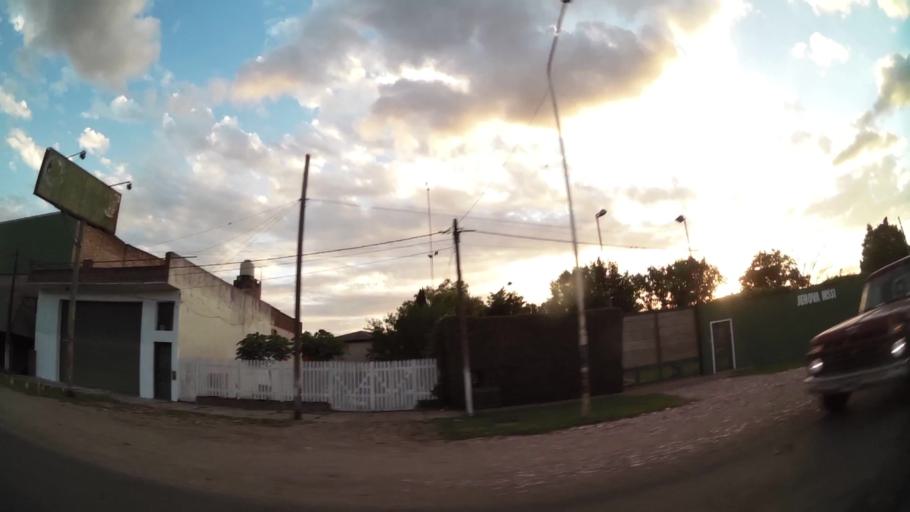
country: AR
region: Buenos Aires
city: Santa Catalina - Dique Lujan
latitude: -34.4907
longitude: -58.7680
